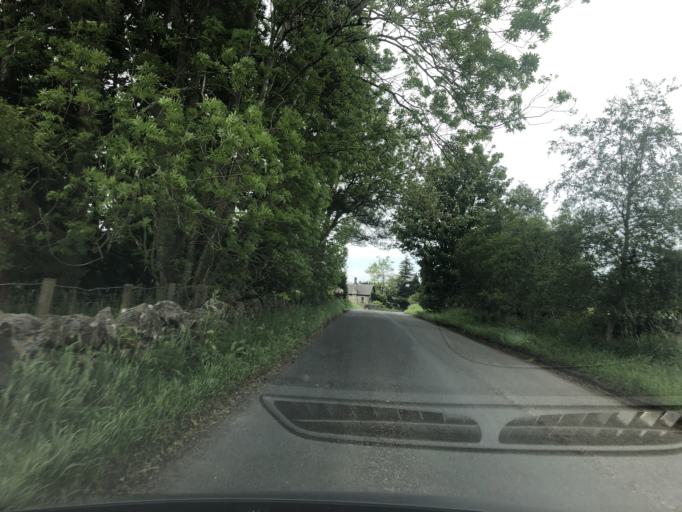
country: GB
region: Scotland
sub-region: The Scottish Borders
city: West Linton
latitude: 55.7342
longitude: -3.3306
